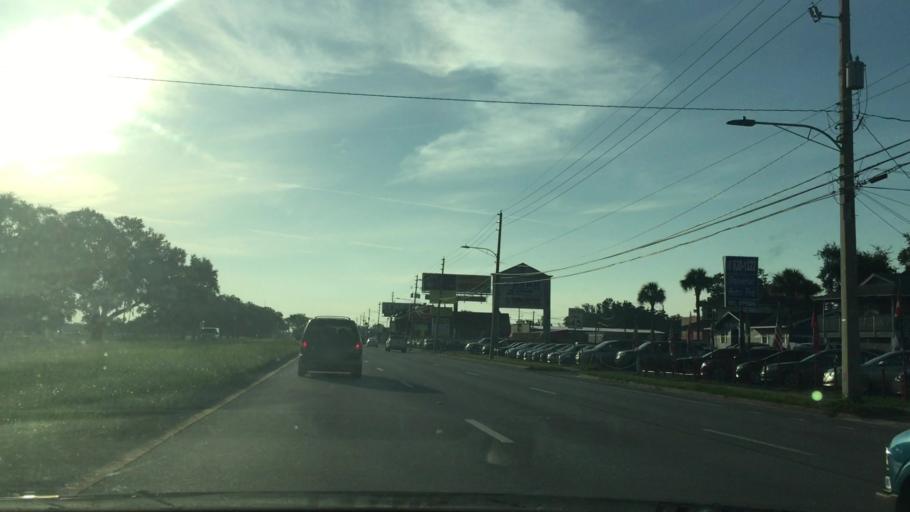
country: US
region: Florida
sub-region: Orange County
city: Pine Hills
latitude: 28.5525
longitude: -81.4381
